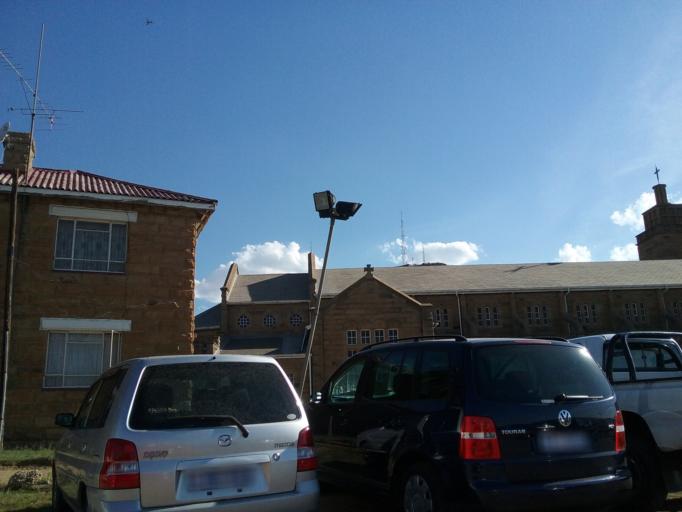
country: LS
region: Maseru
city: Maseru
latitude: -29.3166
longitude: 27.4953
